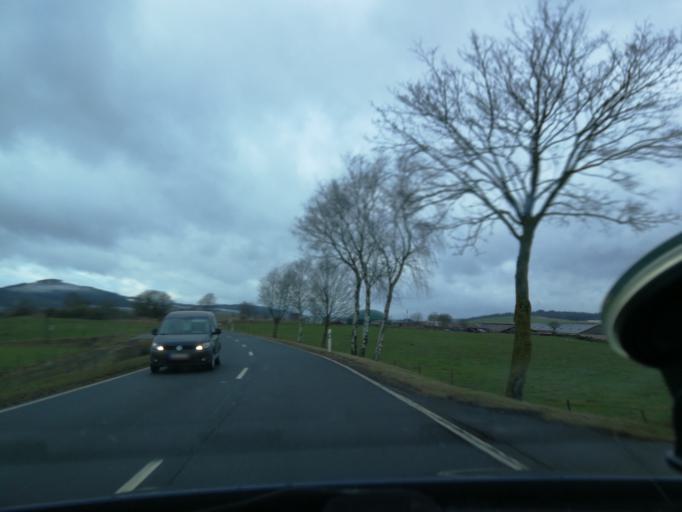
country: DE
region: Rheinland-Pfalz
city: Dreis-Bruck
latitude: 50.2579
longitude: 6.8024
